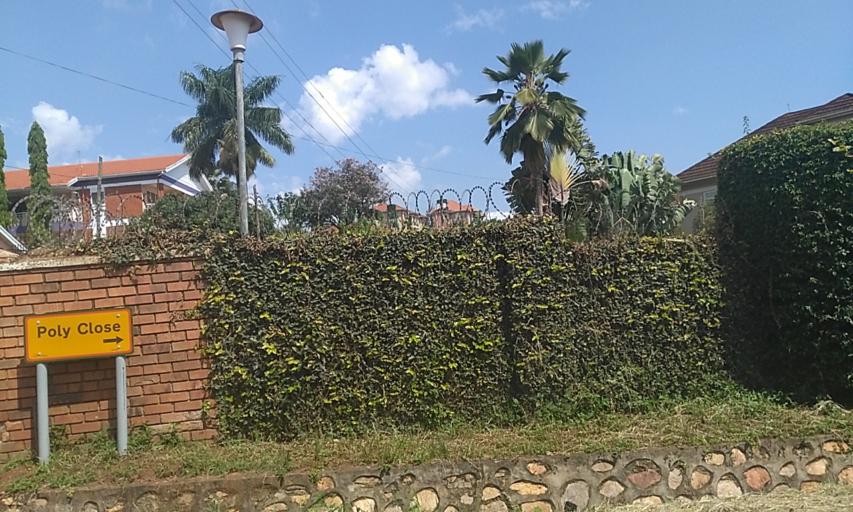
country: UG
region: Central Region
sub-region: Wakiso District
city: Kireka
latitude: 0.3559
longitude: 32.6193
